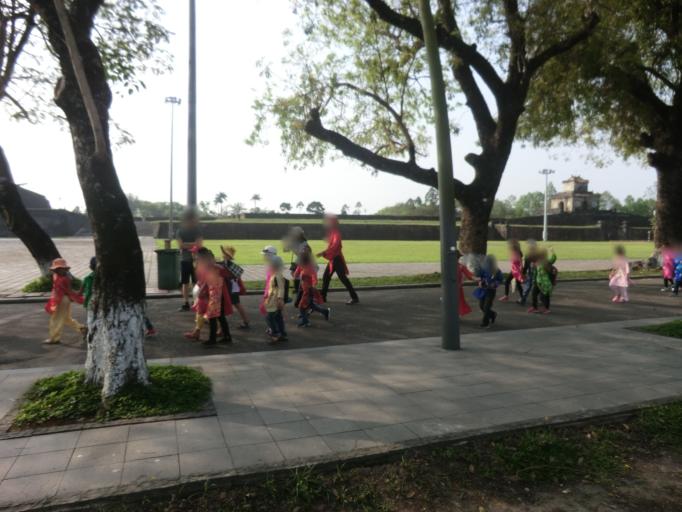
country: VN
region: Thua Thien-Hue
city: Hue
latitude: 16.4669
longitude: 107.5789
